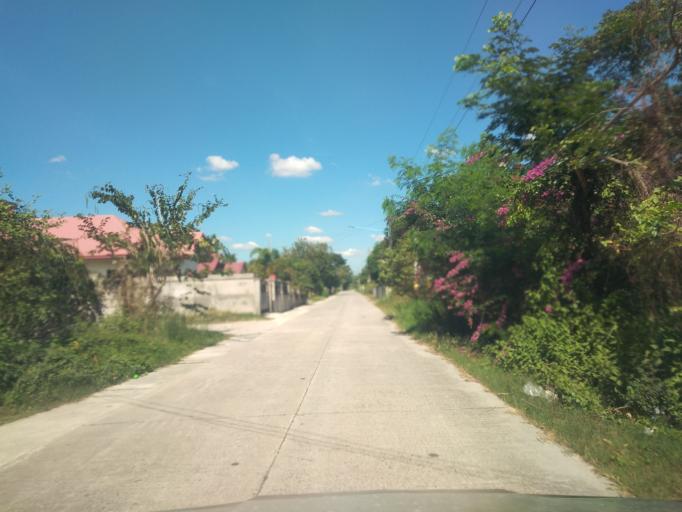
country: PH
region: Central Luzon
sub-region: Province of Pampanga
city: Santa Rita
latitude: 15.0320
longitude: 120.6244
